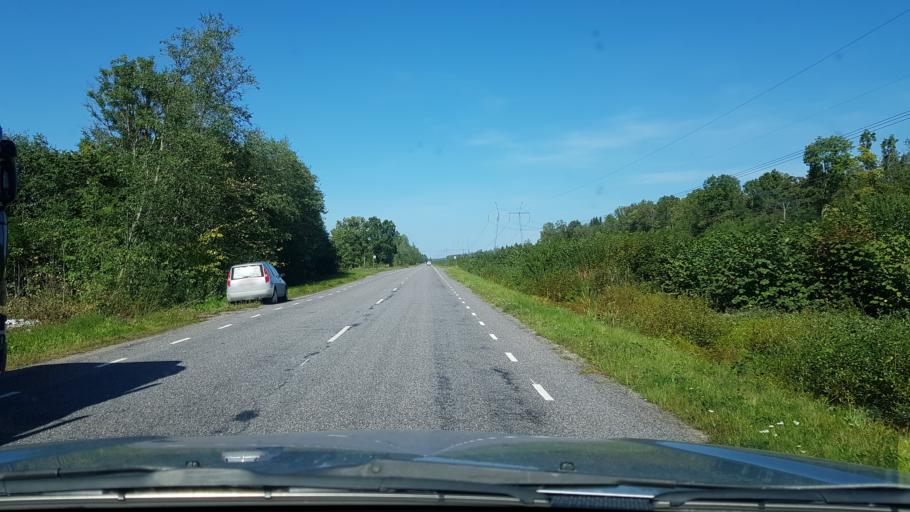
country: EE
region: Ida-Virumaa
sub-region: Sillamaee linn
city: Sillamae
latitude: 59.3341
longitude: 27.7605
